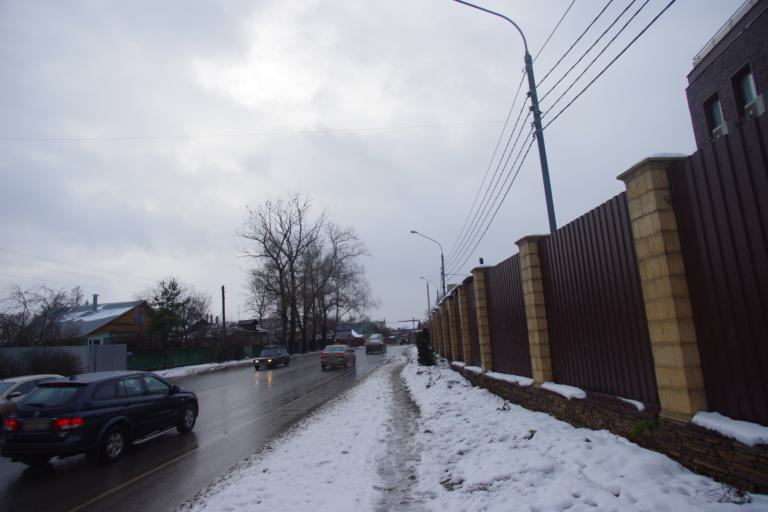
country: RU
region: Moskovskaya
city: Arkhangel'skoye
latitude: 55.8006
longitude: 37.3159
